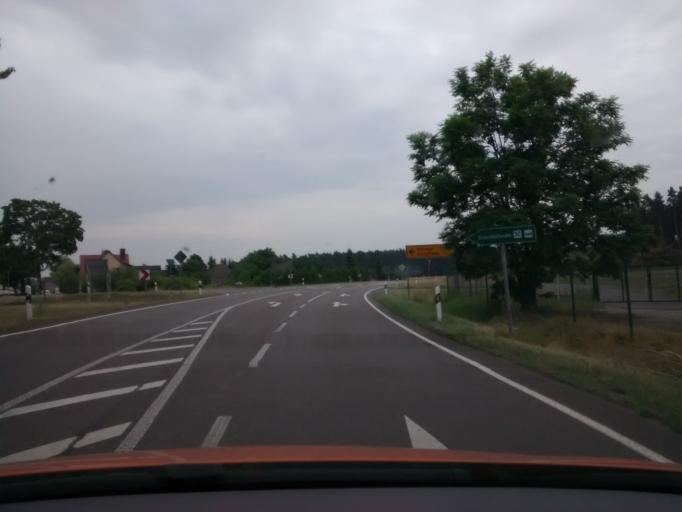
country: DE
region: Brandenburg
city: Wiesenburg
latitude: 52.0888
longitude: 12.4444
